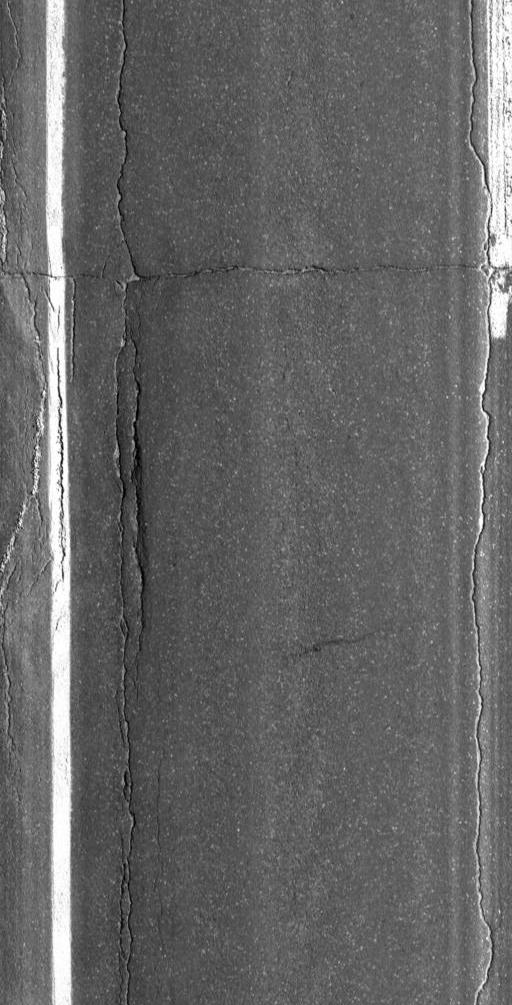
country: US
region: Vermont
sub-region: Caledonia County
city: Saint Johnsbury
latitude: 44.3358
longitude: -72.0424
